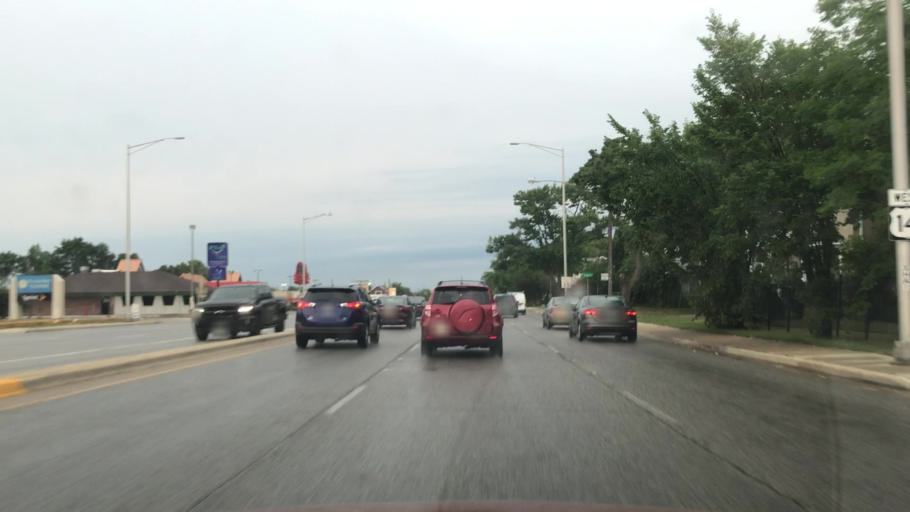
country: US
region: Illinois
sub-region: Cook County
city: Morton Grove
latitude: 42.0409
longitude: -87.7997
